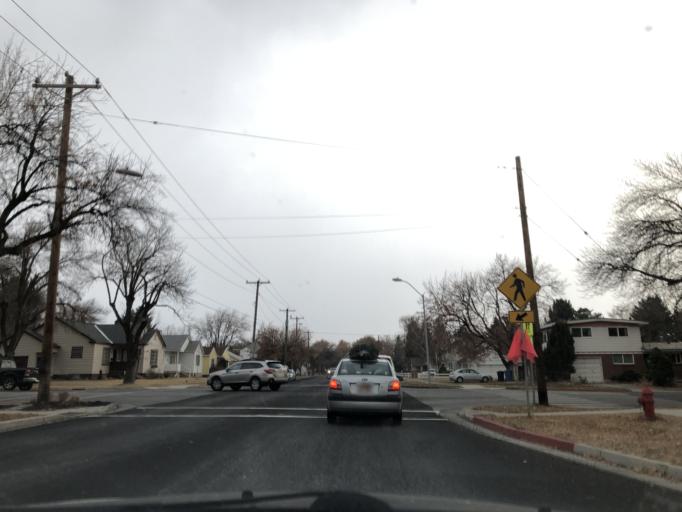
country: US
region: Utah
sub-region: Cache County
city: Logan
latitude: 41.7450
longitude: -111.8295
